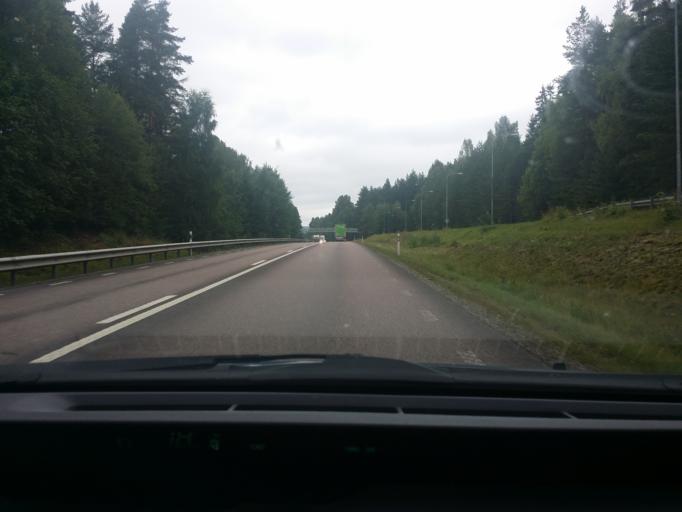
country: SE
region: Dalarna
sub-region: Borlange Kommun
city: Borlaenge
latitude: 60.5093
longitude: 15.3839
